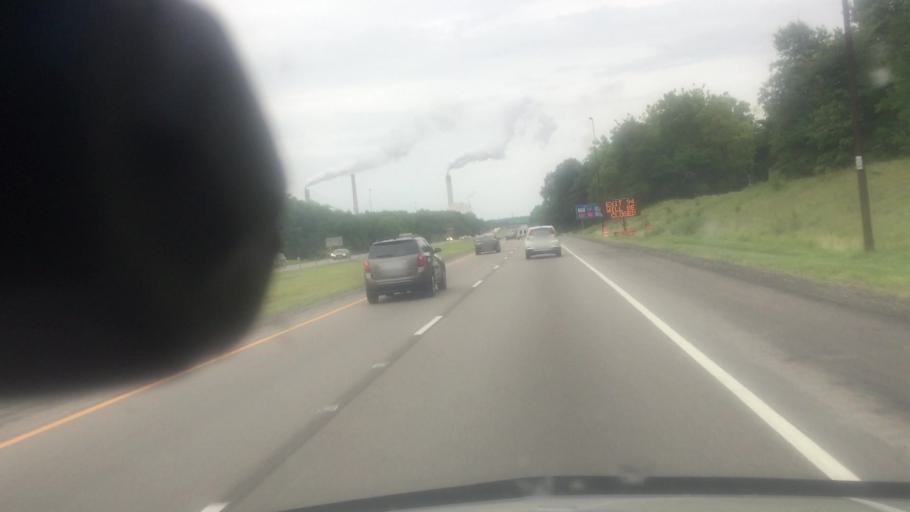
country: US
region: Illinois
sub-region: Sangamon County
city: Grandview
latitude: 39.7736
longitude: -89.6029
